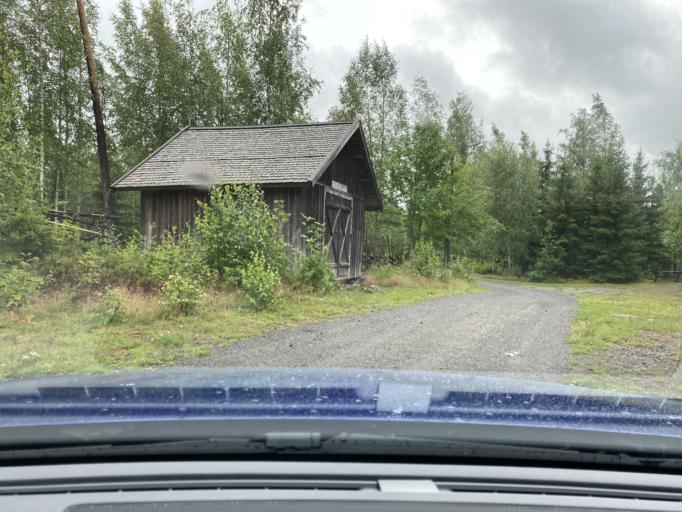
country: FI
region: Pirkanmaa
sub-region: Lounais-Pirkanmaa
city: Punkalaidun
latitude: 61.1108
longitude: 23.1348
